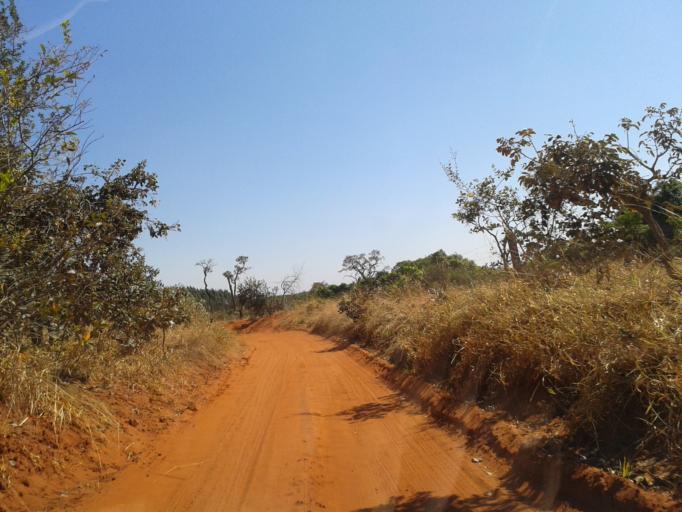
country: BR
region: Minas Gerais
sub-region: Ituiutaba
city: Ituiutaba
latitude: -19.0153
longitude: -49.2171
